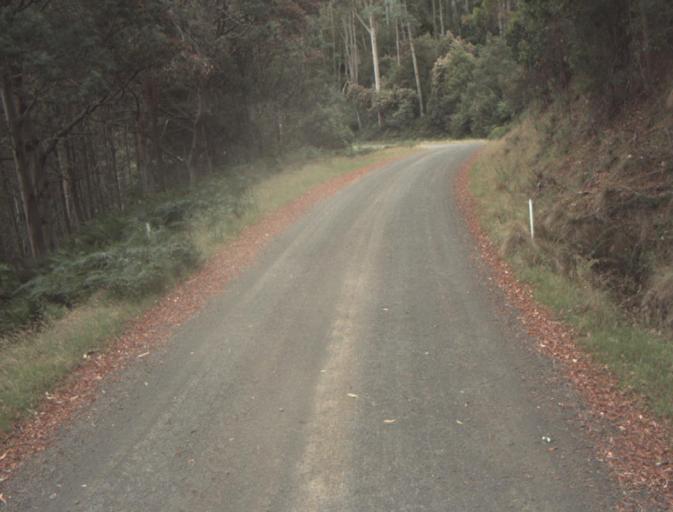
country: AU
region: Tasmania
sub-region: Dorset
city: Scottsdale
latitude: -41.4450
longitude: 147.5889
